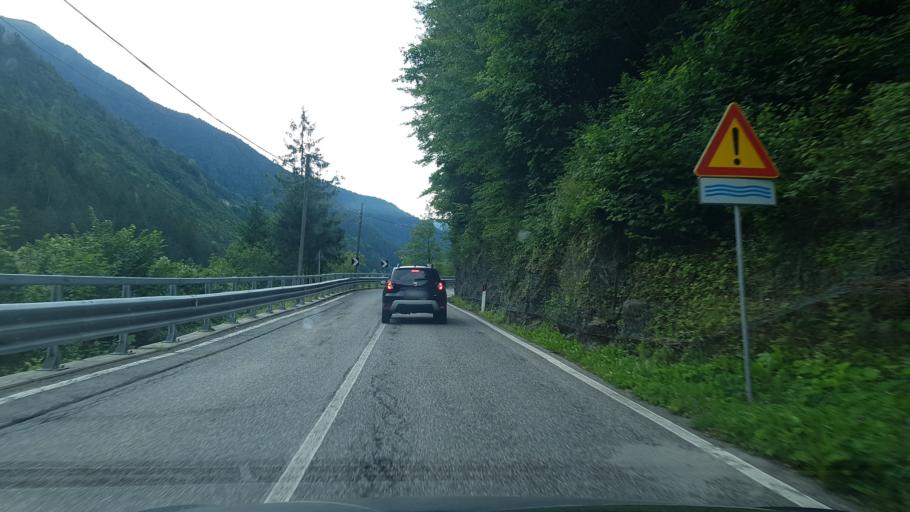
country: IT
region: Friuli Venezia Giulia
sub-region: Provincia di Udine
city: Rigolato
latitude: 46.5630
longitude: 12.8434
